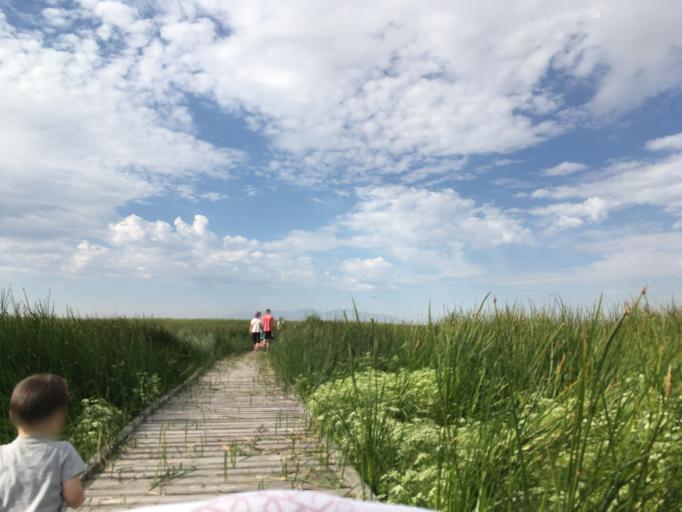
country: US
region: Utah
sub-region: Davis County
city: Layton
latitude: 41.0378
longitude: -112.0237
